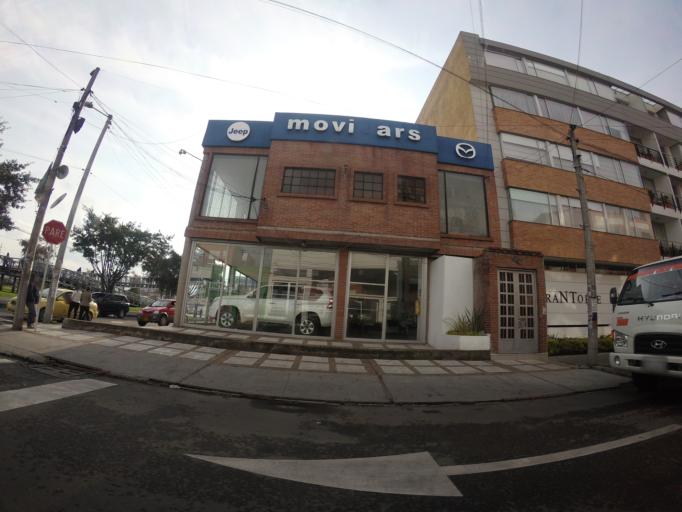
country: CO
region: Bogota D.C.
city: Barrio San Luis
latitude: 4.7046
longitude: -74.0552
